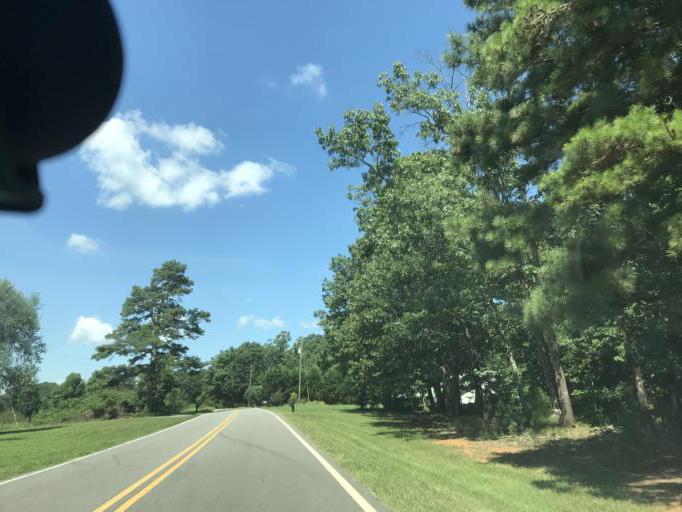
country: US
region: Georgia
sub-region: Dawson County
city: Dawsonville
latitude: 34.3134
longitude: -84.0215
